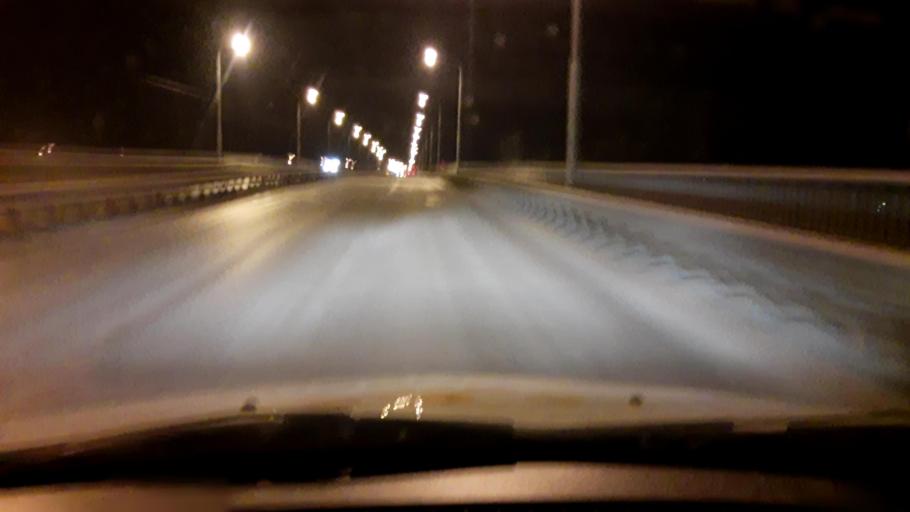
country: RU
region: Bashkortostan
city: Iglino
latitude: 54.7887
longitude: 56.2162
